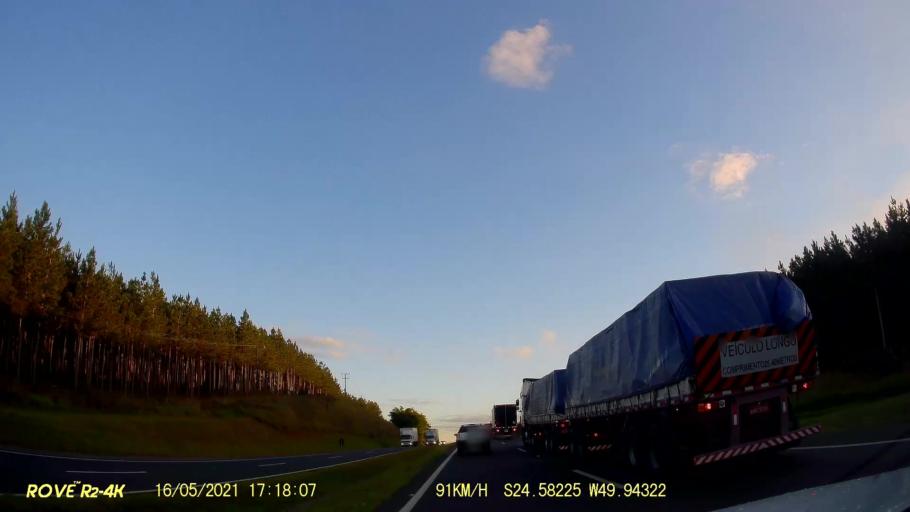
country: BR
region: Parana
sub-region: Pirai Do Sul
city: Pirai do Sul
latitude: -24.5825
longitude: -49.9433
